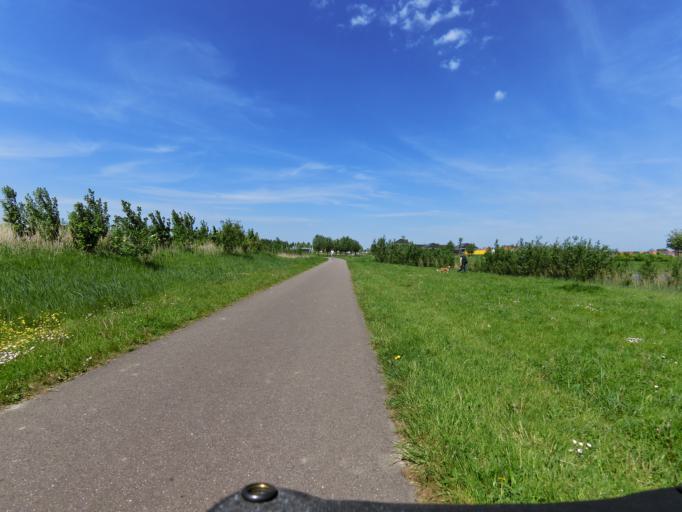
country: NL
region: South Holland
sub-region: Gemeente Barendrecht
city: Barendrecht
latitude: 51.8418
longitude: 4.5201
